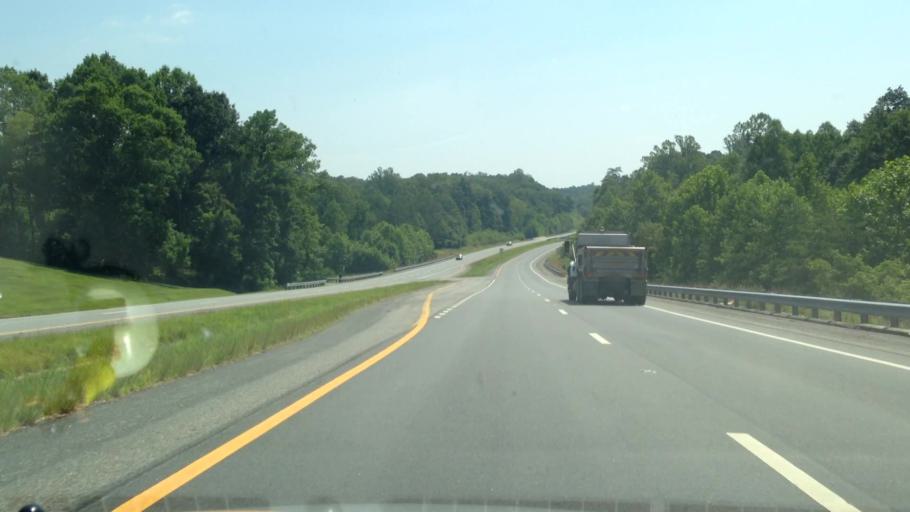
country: US
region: Virginia
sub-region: Patrick County
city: Patrick Springs
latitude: 36.5902
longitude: -80.1223
